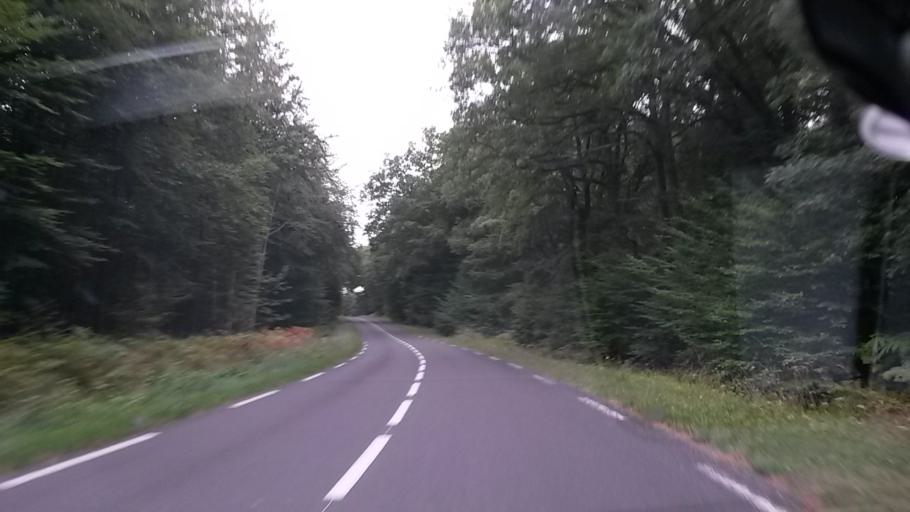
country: FR
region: Haute-Normandie
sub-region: Departement de l'Eure
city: Charleval
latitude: 49.3675
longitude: 1.4618
